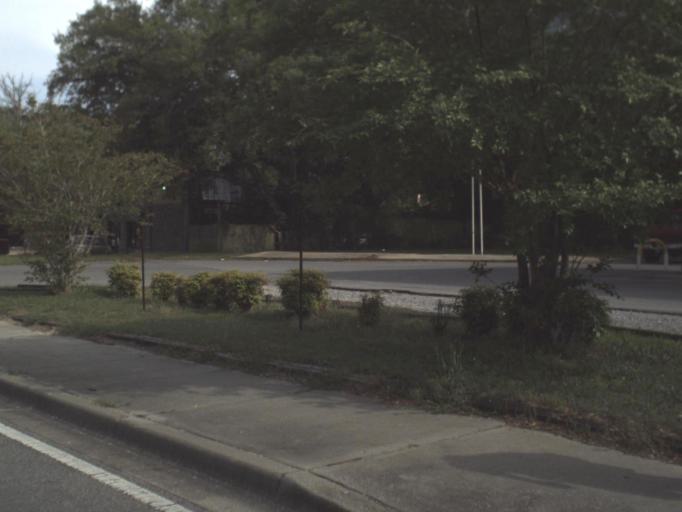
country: US
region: Florida
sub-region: Escambia County
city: Ferry Pass
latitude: 30.4960
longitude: -87.2131
